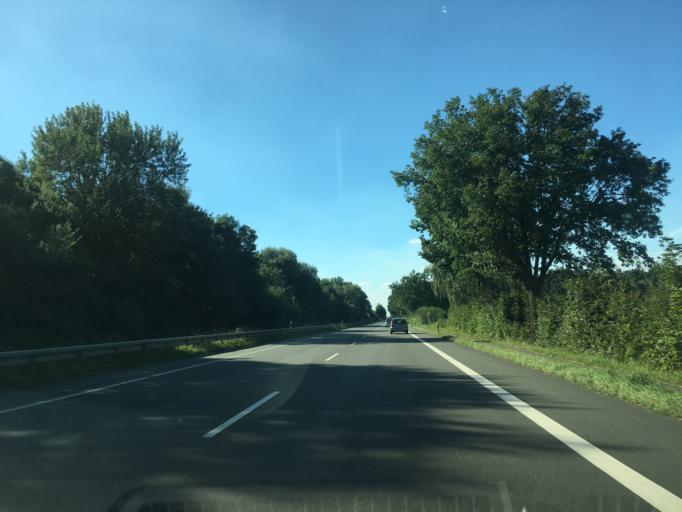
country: DE
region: North Rhine-Westphalia
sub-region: Regierungsbezirk Detmold
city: Harsewinkel
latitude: 51.8906
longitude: 8.2177
